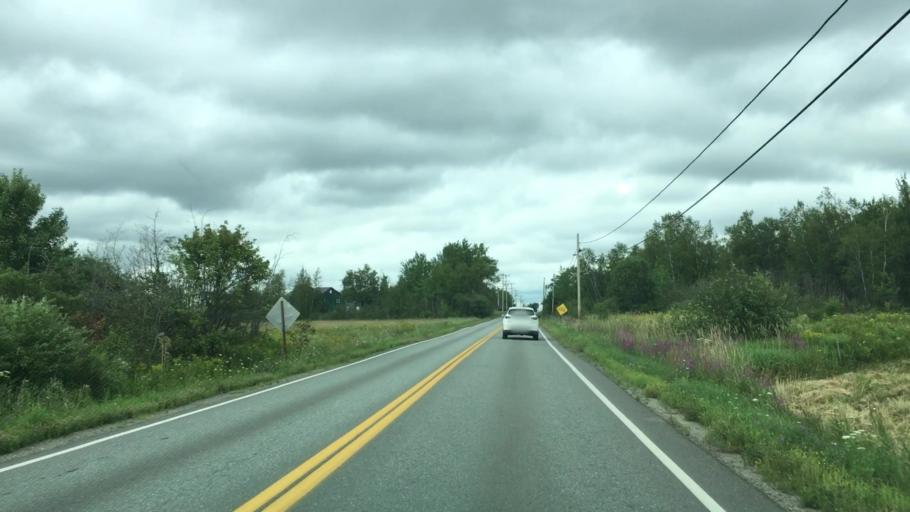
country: US
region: Maine
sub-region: Penobscot County
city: Brewer
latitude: 44.7666
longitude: -68.7492
